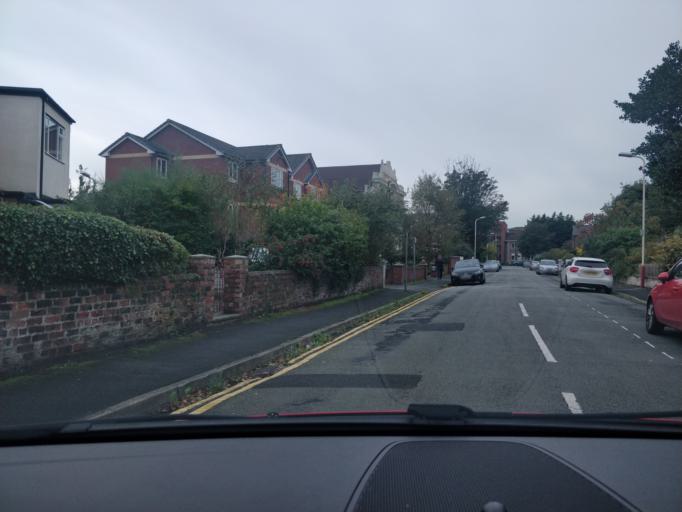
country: GB
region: England
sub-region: Sefton
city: Southport
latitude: 53.6499
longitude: -2.9949
